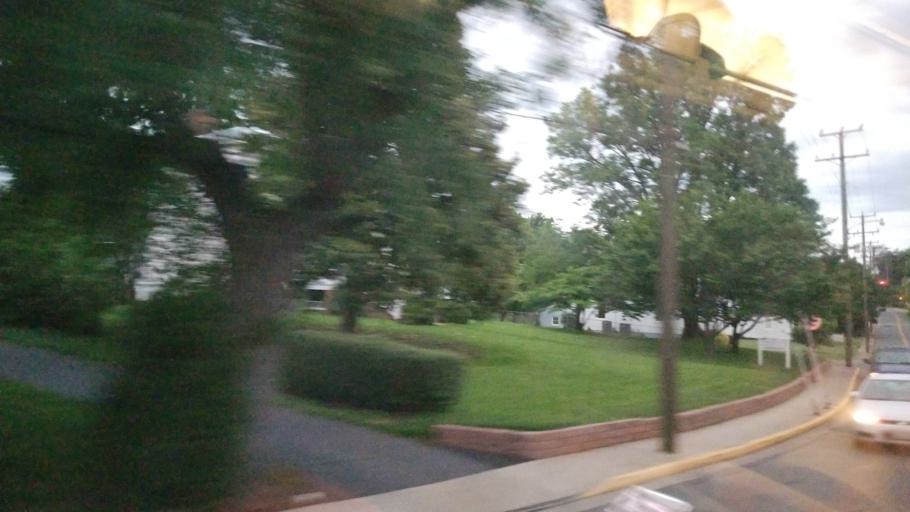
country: US
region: Virginia
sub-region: Orange County
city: Orange
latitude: 38.2473
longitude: -78.1104
